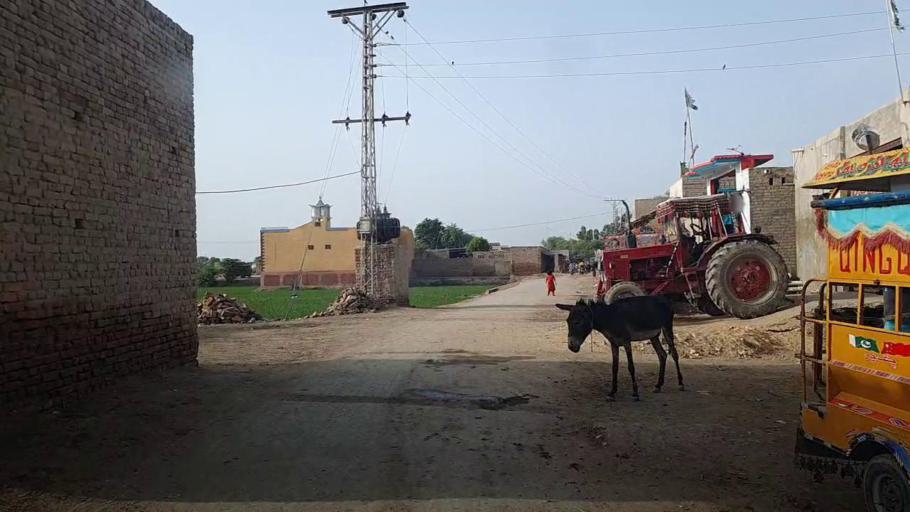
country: PK
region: Sindh
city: Khairpur Nathan Shah
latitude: 27.1149
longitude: 67.7885
